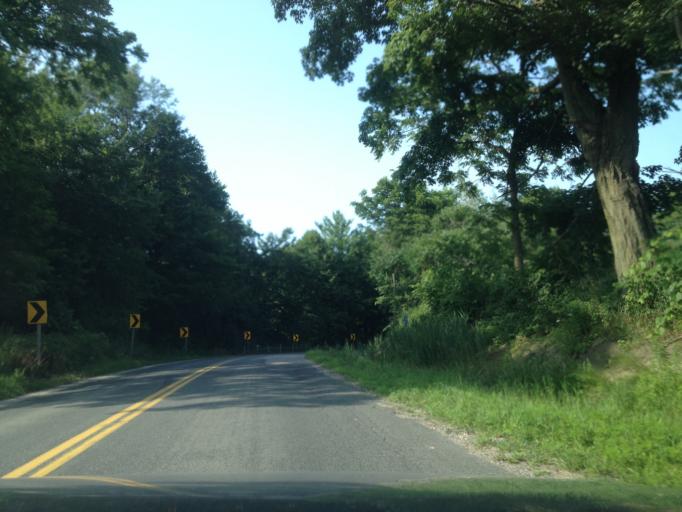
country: CA
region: Ontario
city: Aylmer
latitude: 42.7530
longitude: -80.8502
